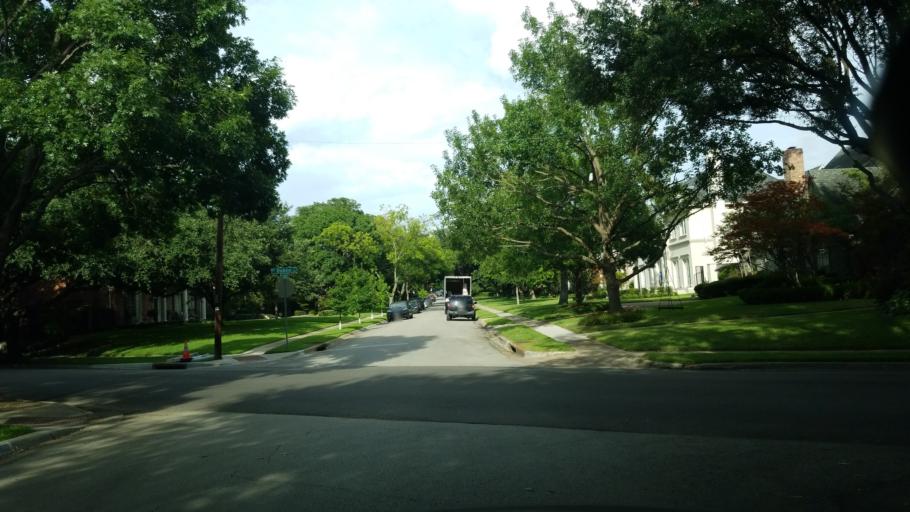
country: US
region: Texas
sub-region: Dallas County
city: University Park
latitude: 32.8530
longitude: -96.7797
